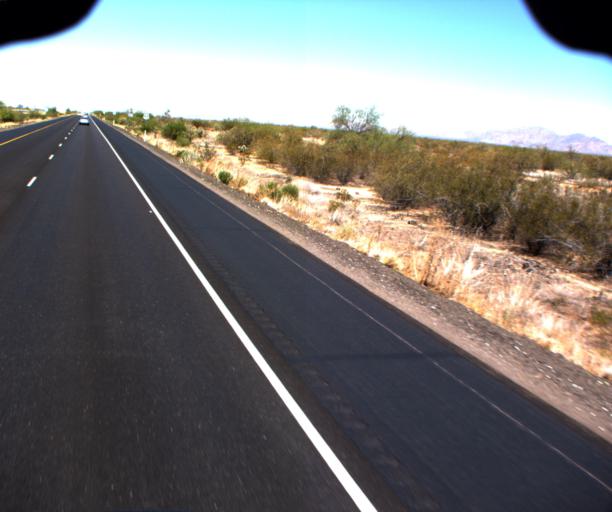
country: US
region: Arizona
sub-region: Yavapai County
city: Congress
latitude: 34.0798
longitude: -112.8879
